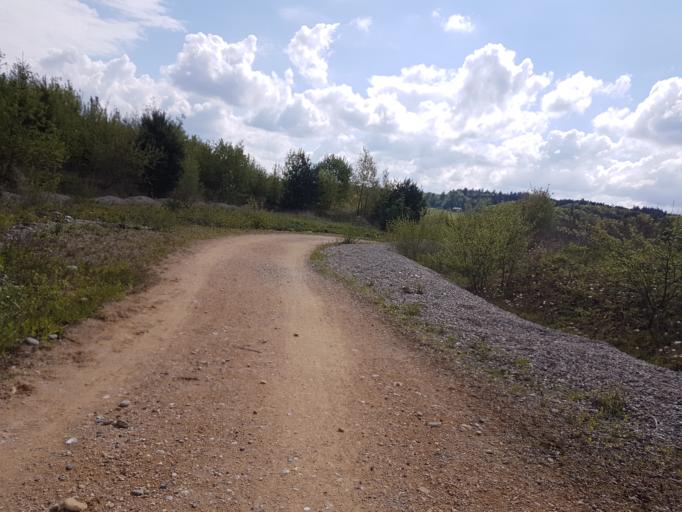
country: CH
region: Solothurn
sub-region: Bezirk Olten
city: Gunzgen
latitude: 47.2968
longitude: 7.8461
